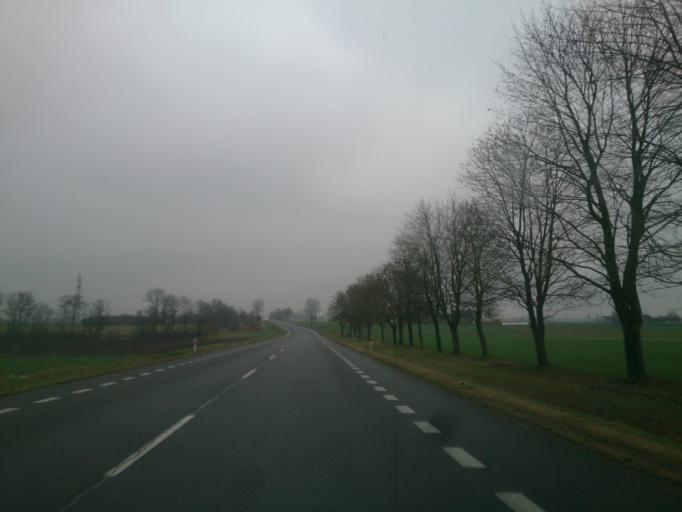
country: PL
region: Masovian Voivodeship
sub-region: Powiat plocki
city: Drobin
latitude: 52.7277
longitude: 20.0072
